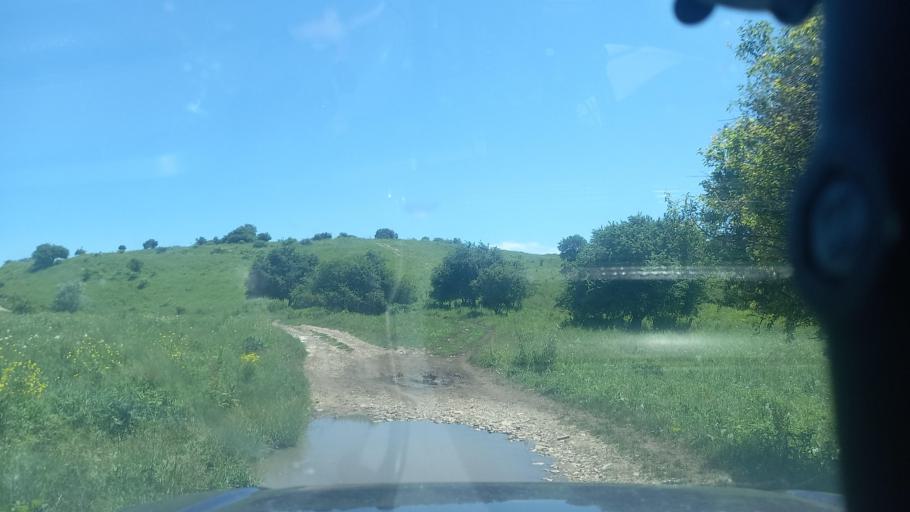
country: RU
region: Karachayevo-Cherkesiya
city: Pregradnaya
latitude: 44.1025
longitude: 41.1195
